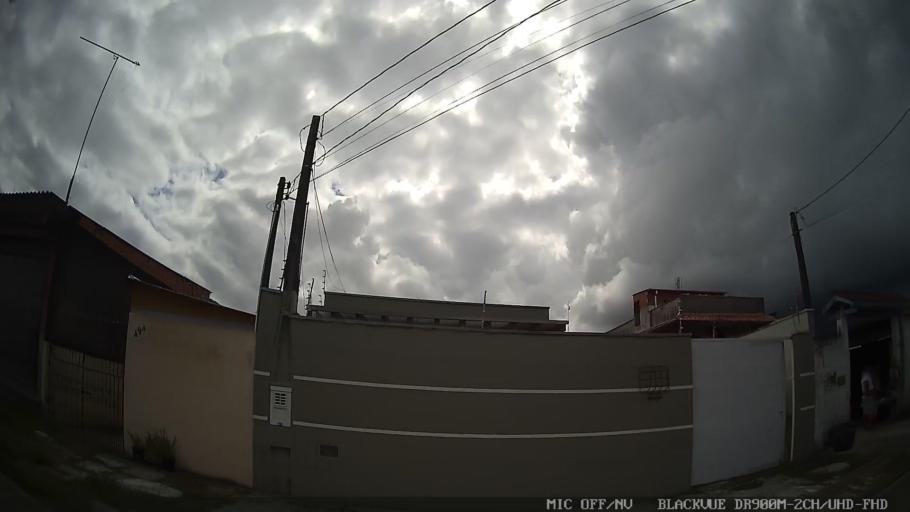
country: BR
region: Sao Paulo
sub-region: Caraguatatuba
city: Caraguatatuba
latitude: -23.6413
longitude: -45.4348
